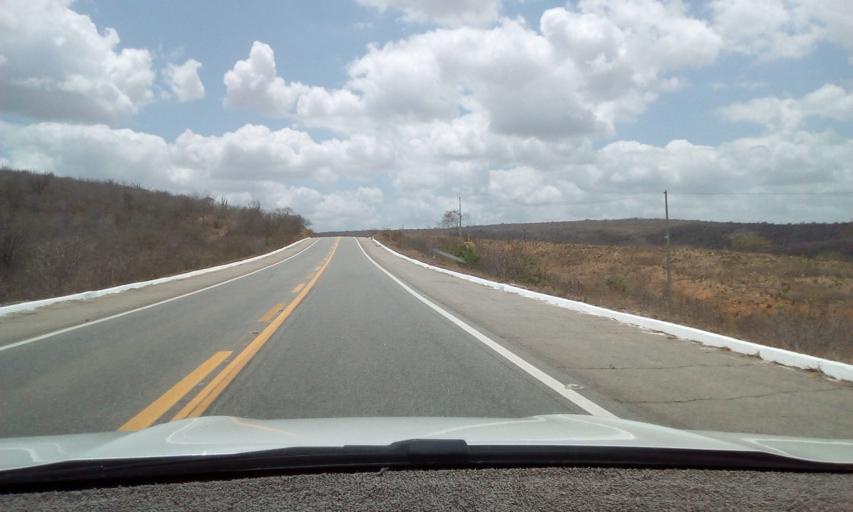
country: BR
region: Paraiba
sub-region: Boqueirao
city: Boqueirao
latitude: -7.6782
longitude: -36.0666
